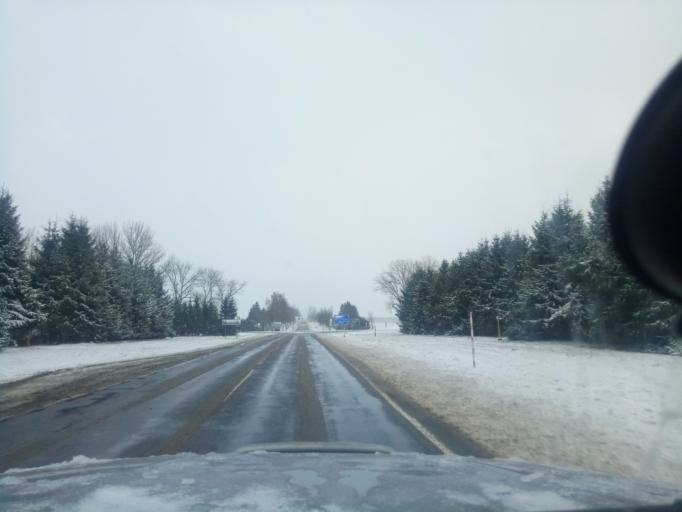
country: BY
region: Minsk
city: Haradzyeya
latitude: 53.3616
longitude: 26.5138
